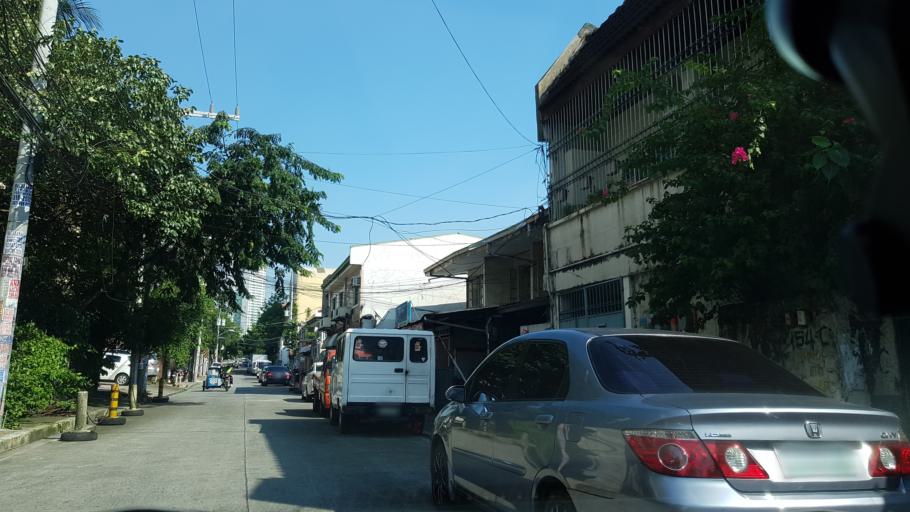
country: PH
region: Metro Manila
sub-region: Quezon City
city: Quezon City
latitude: 14.6246
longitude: 121.0438
